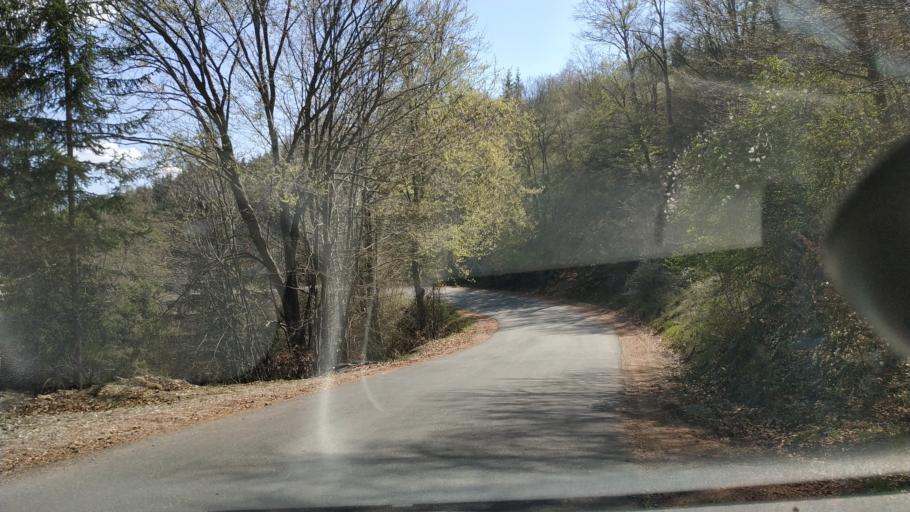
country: RS
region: Central Serbia
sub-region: Zajecarski Okrug
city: Soko Banja
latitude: 43.5878
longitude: 21.8872
